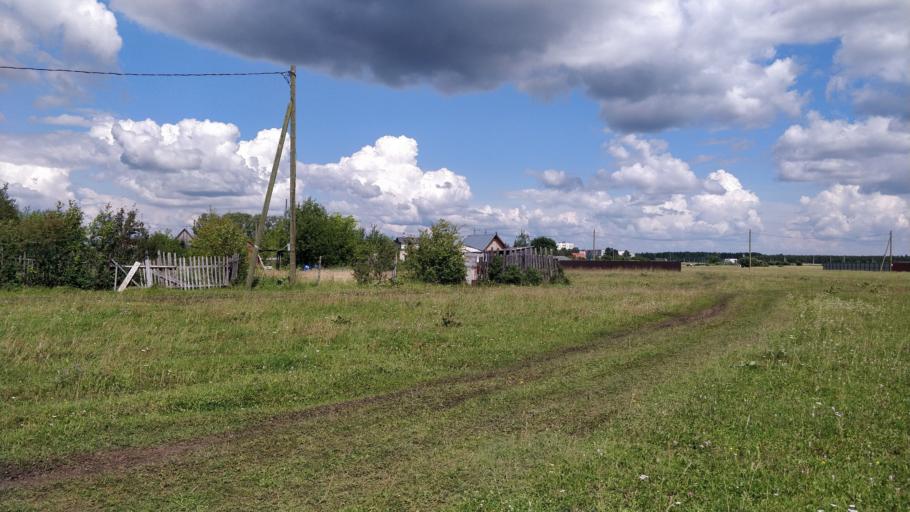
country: RU
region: Perm
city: Ust'-Kachka
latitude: 57.9945
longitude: 55.6632
